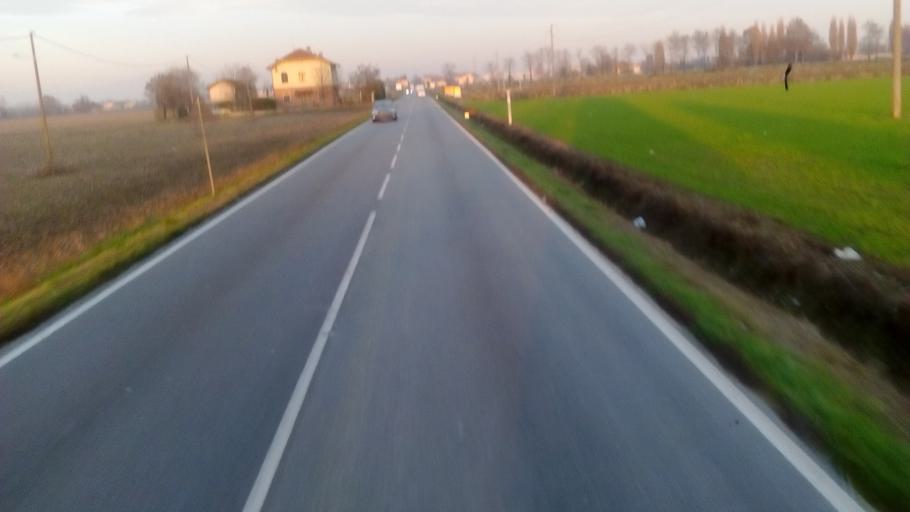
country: IT
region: Lombardy
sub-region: Provincia di Cremona
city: Ticengo
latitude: 45.3801
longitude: 9.8413
